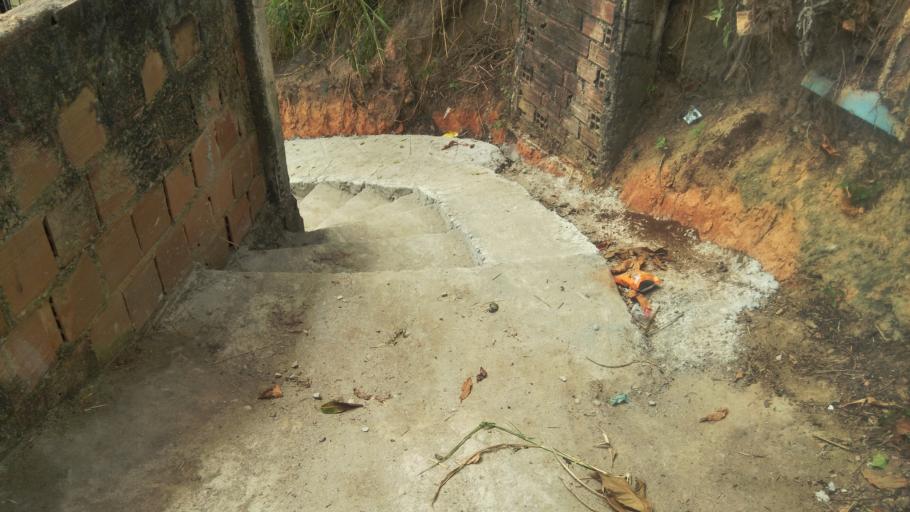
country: BR
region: Pernambuco
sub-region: Jaboatao Dos Guararapes
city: Jaboatao dos Guararapes
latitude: -8.0667
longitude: -34.9977
